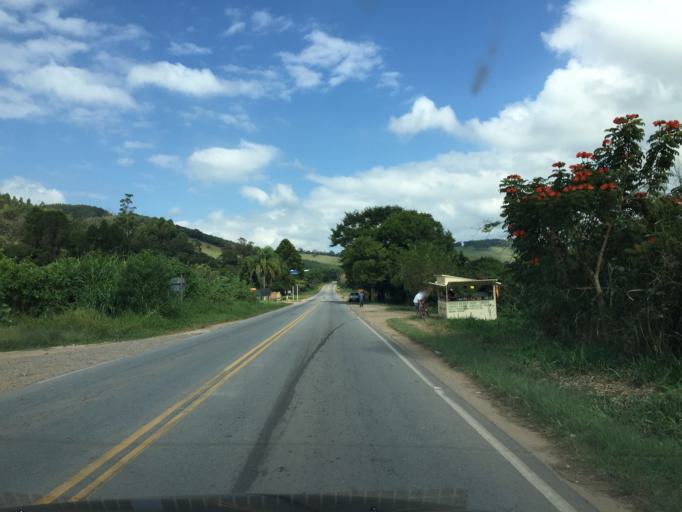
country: BR
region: Minas Gerais
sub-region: Passa Quatro
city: Passa Quatro
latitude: -22.3582
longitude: -44.9513
